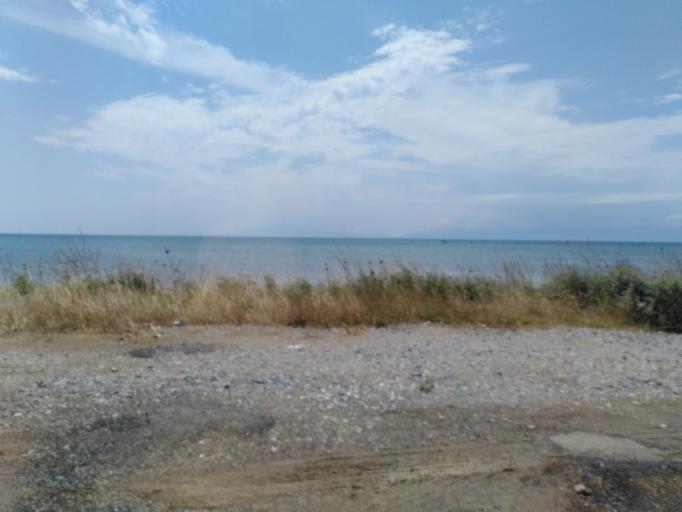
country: GR
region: Central Macedonia
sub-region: Nomos Thessalonikis
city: Nea Michaniona
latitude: 40.4301
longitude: 22.8729
